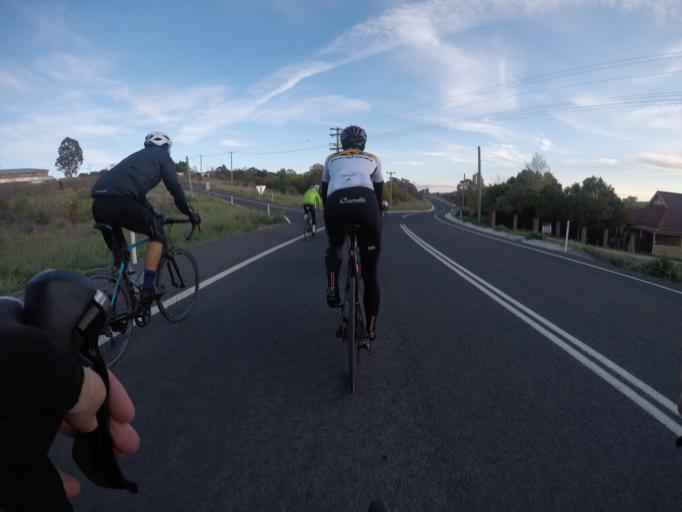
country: AU
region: New South Wales
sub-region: Cabonne
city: Molong
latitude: -33.0881
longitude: 148.8619
